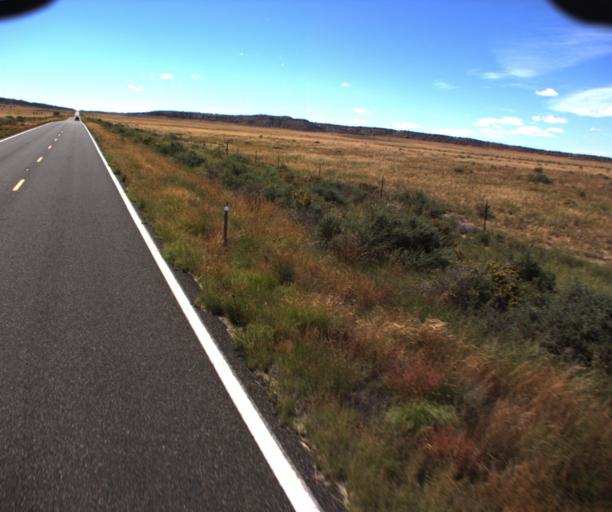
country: US
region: Arizona
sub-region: Apache County
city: Saint Johns
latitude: 34.6801
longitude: -109.2827
